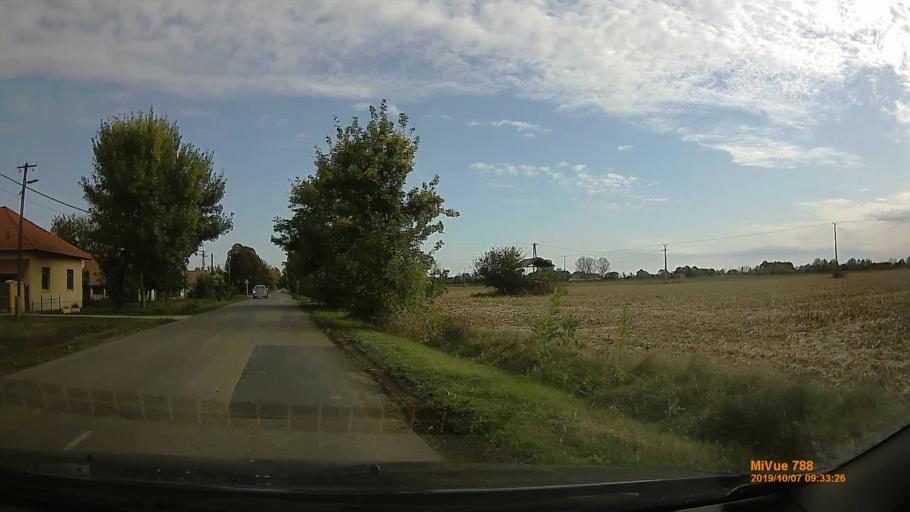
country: HU
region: Bekes
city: Szarvas
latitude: 46.8205
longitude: 20.6582
